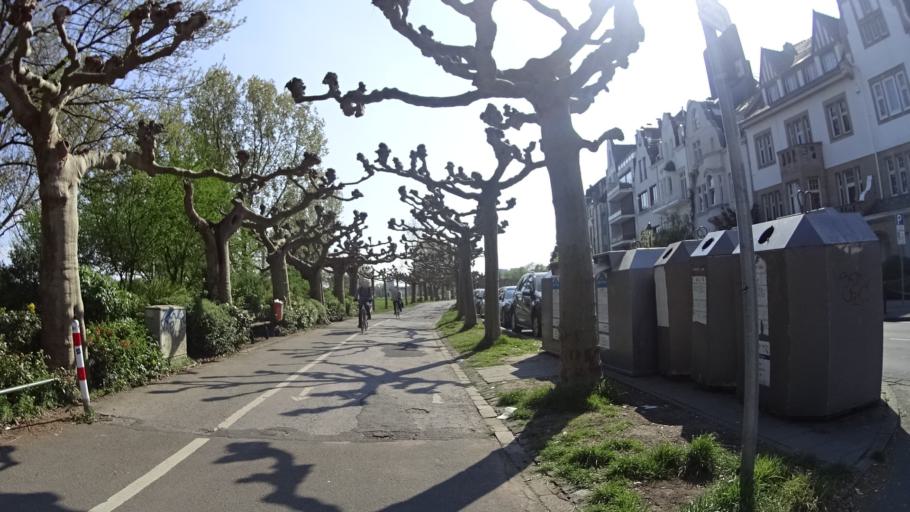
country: DE
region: North Rhine-Westphalia
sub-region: Regierungsbezirk Dusseldorf
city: Dusseldorf
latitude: 51.2293
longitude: 6.7623
